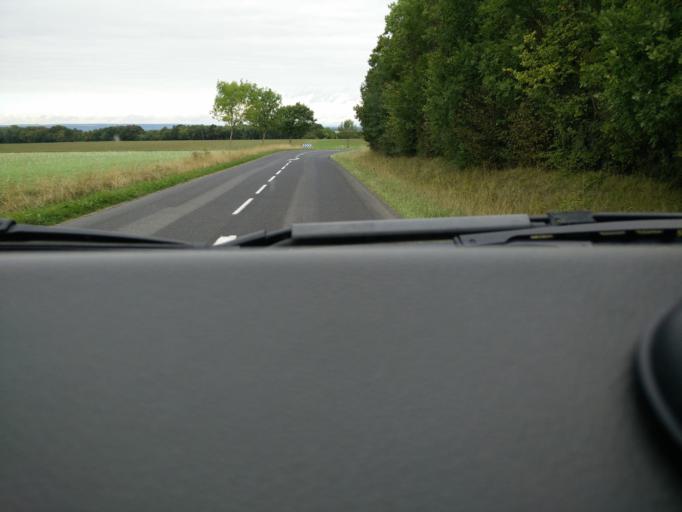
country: FR
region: Lorraine
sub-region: Departement de Meurthe-et-Moselle
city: Montauville
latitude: 48.9334
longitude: 5.8951
